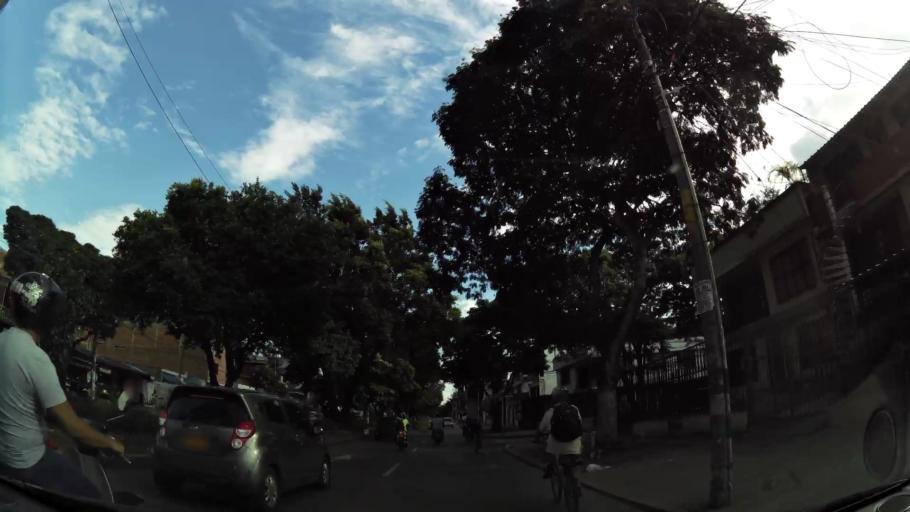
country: CO
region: Valle del Cauca
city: Cali
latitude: 3.4603
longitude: -76.5071
